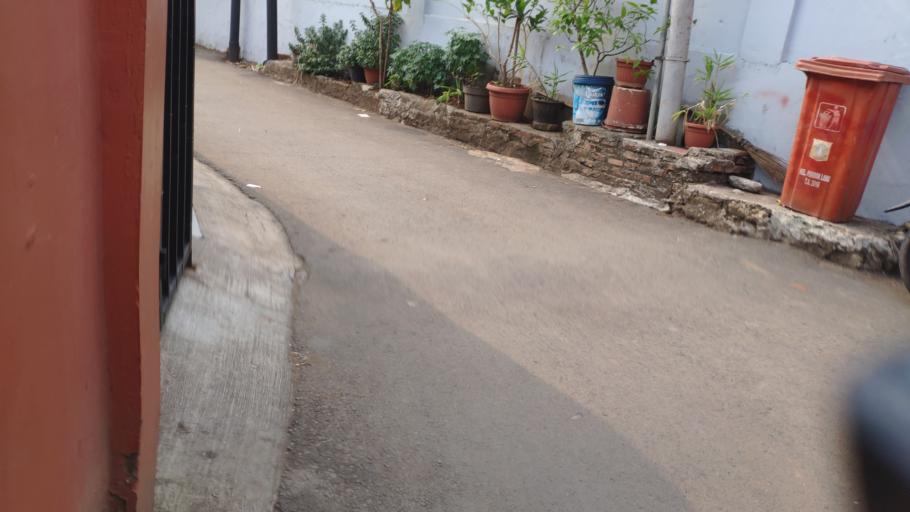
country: ID
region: West Java
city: Pamulang
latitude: -6.3146
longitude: 106.8050
